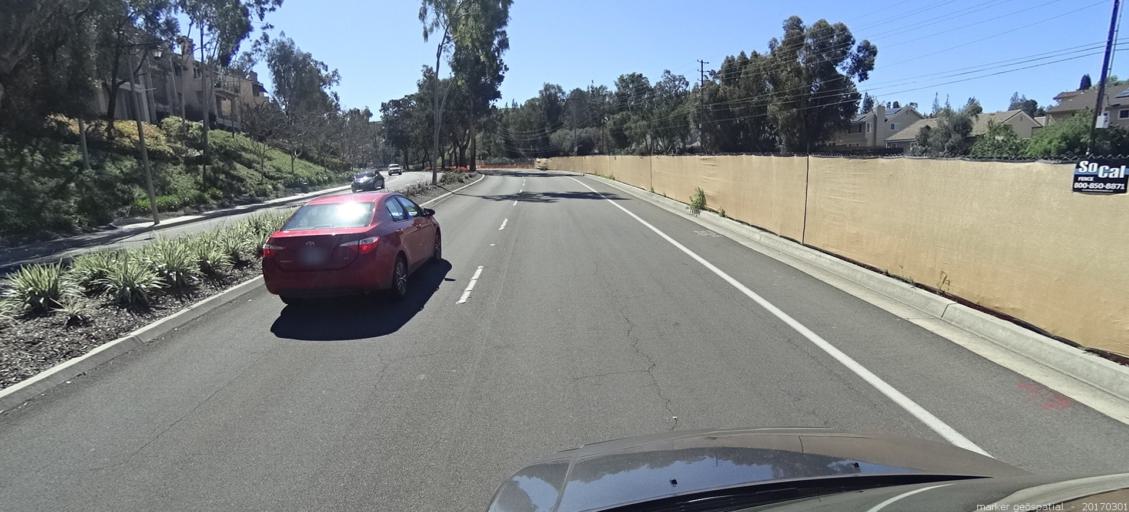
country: US
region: California
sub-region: Orange County
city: Villa Park
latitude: 33.8495
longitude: -117.7788
